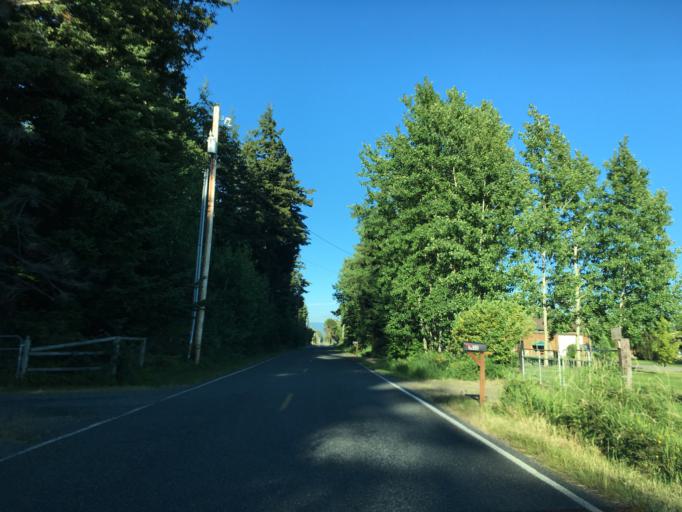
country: US
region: Washington
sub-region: Whatcom County
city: Ferndale
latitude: 48.9063
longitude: -122.6139
